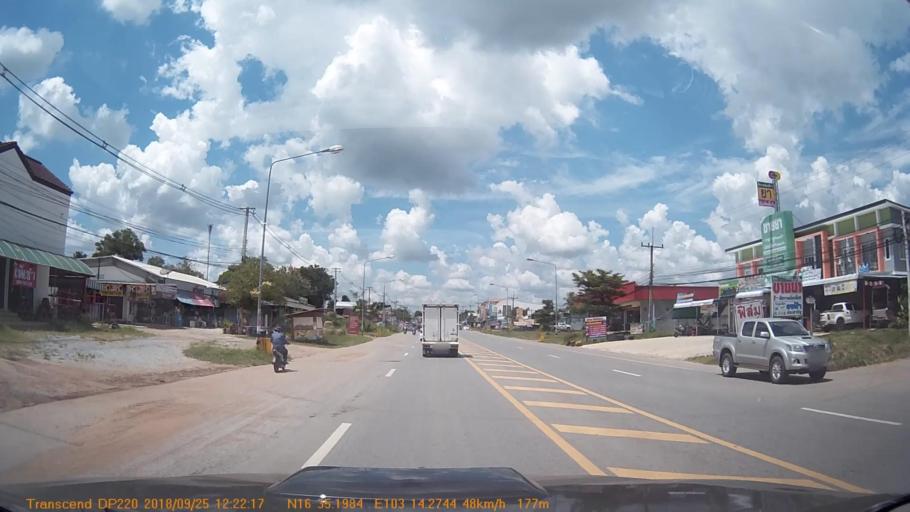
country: TH
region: Kalasin
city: Huai Mek
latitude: 16.5866
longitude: 103.2380
